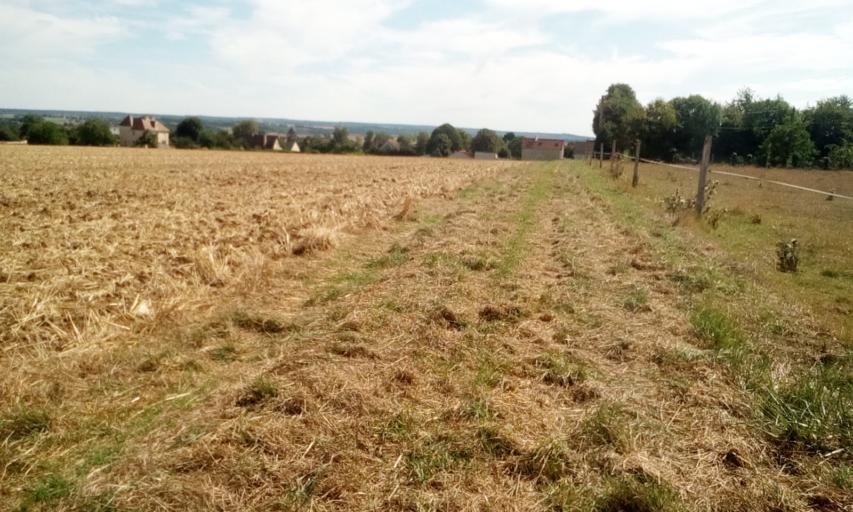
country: FR
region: Lower Normandy
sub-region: Departement du Calvados
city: Bully
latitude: 49.1141
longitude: -0.4321
